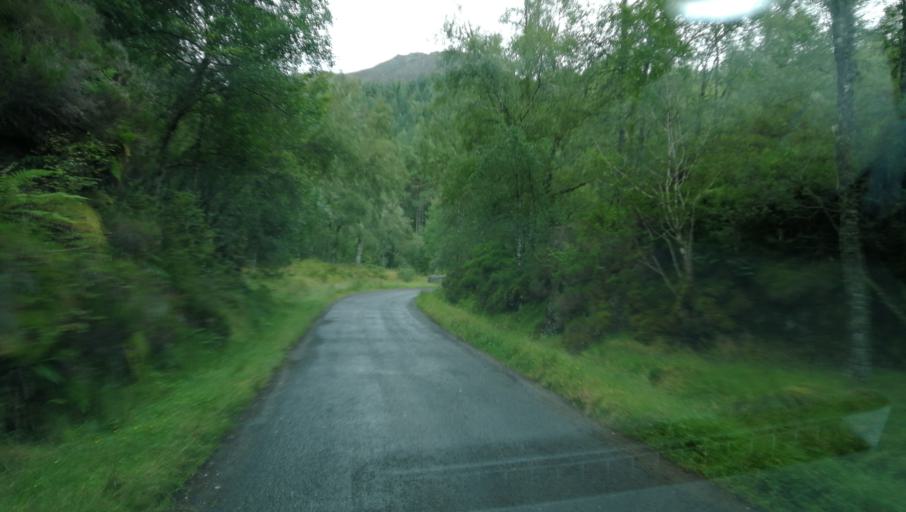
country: GB
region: Scotland
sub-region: Highland
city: Spean Bridge
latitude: 57.3042
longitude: -4.8742
